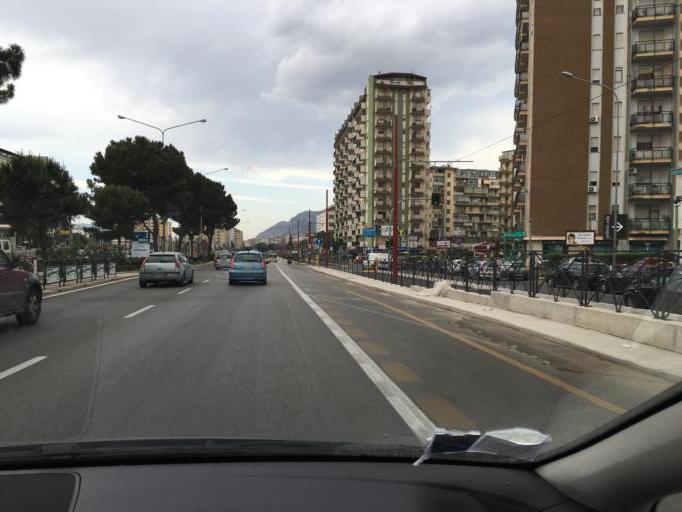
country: IT
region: Sicily
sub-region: Palermo
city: Palermo
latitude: 38.1256
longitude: 13.3295
